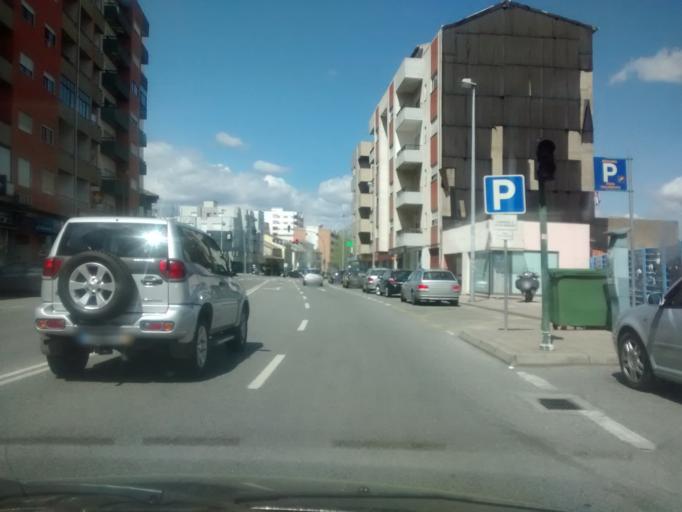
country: PT
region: Braganca
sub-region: Braganca Municipality
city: Braganca
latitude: 41.8032
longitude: -6.7604
